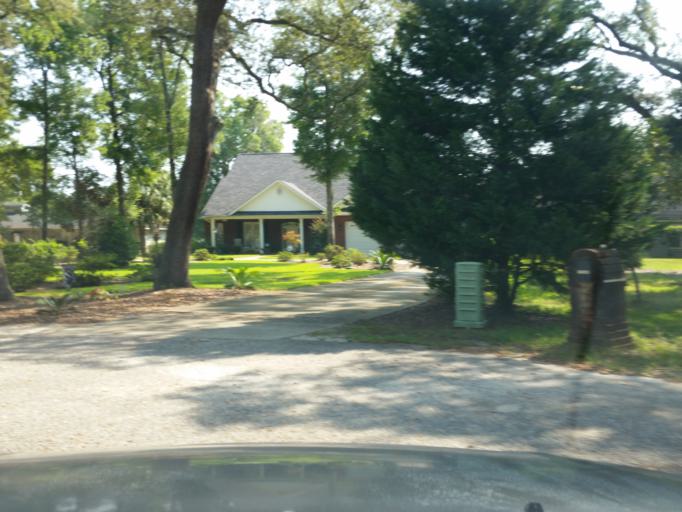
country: US
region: Florida
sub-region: Escambia County
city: Bellview
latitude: 30.5096
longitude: -87.4492
